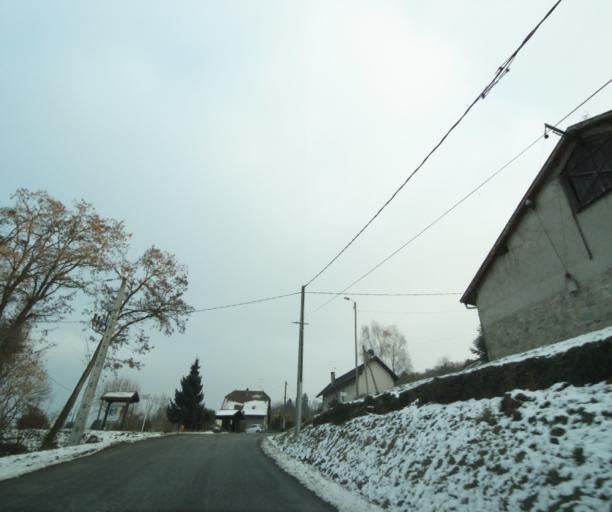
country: FR
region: Rhone-Alpes
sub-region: Departement de la Haute-Savoie
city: Vetraz-Monthoux
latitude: 46.1568
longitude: 6.2368
